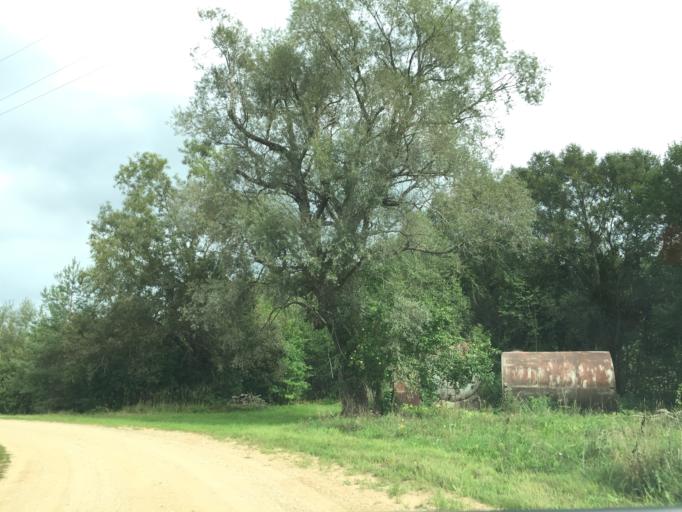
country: LV
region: Pargaujas
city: Stalbe
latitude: 57.5142
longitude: 24.9174
